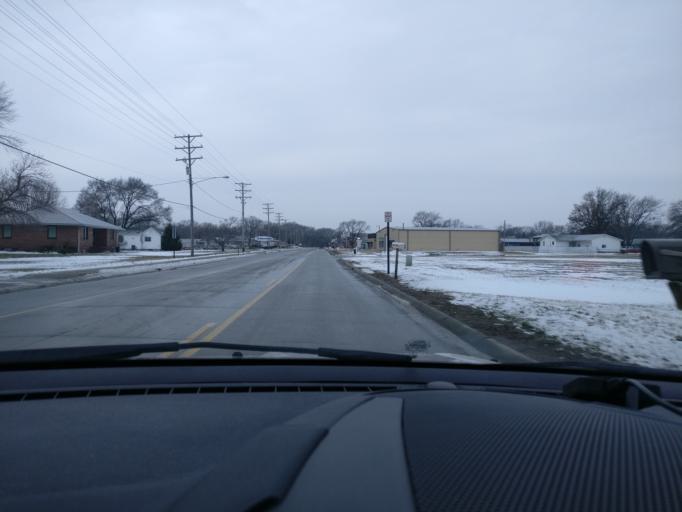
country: US
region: Nebraska
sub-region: Dodge County
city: Fremont
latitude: 41.4368
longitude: -96.5136
